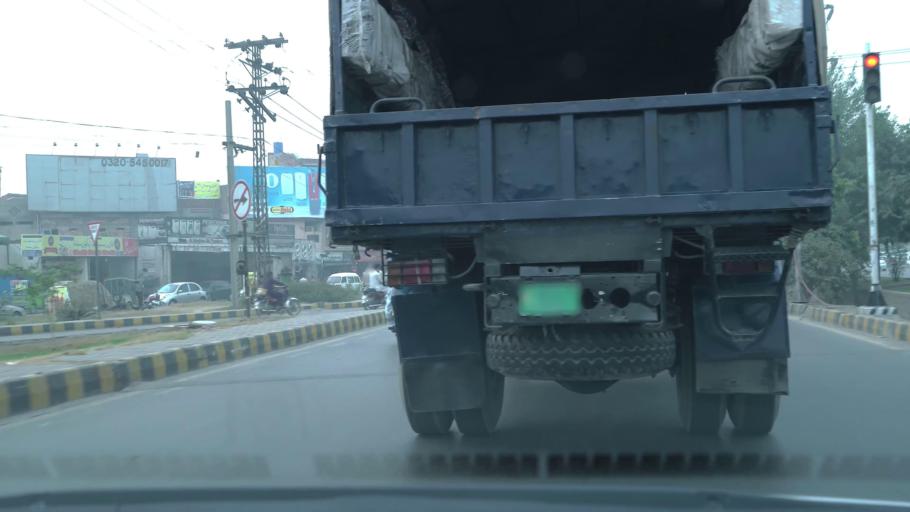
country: PK
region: Punjab
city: Lahore
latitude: 31.4777
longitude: 74.3011
